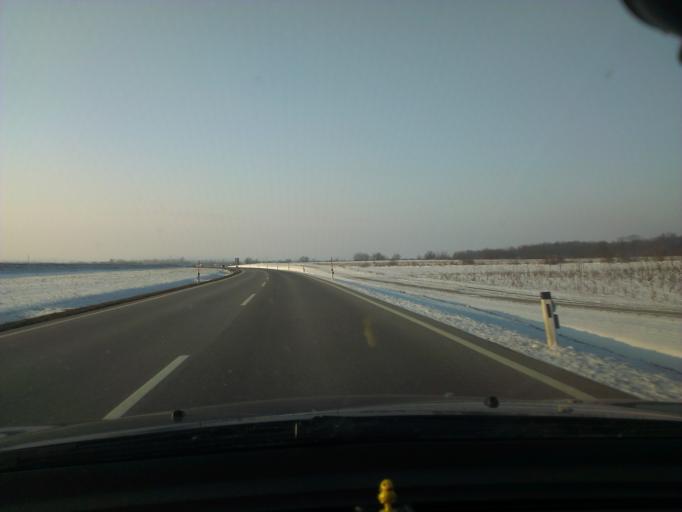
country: AT
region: Burgenland
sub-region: Eisenstadt-Umgebung
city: Schutzen am Gebirge
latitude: 47.8550
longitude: 16.6066
